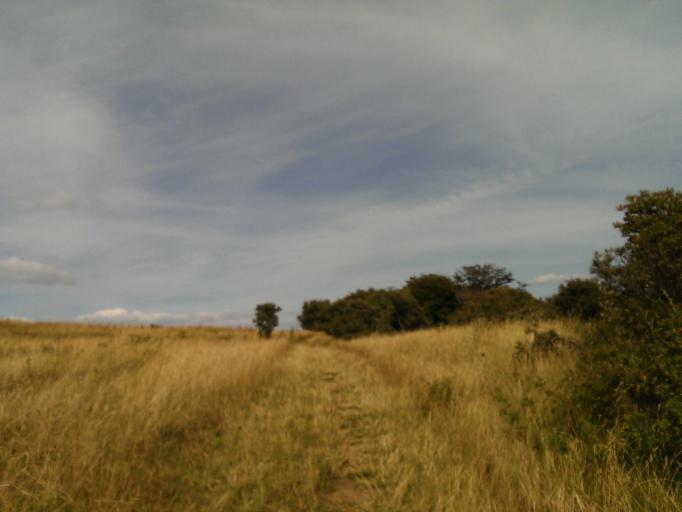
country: DK
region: Central Jutland
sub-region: Syddjurs Kommune
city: Ebeltoft
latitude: 56.1009
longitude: 10.5329
